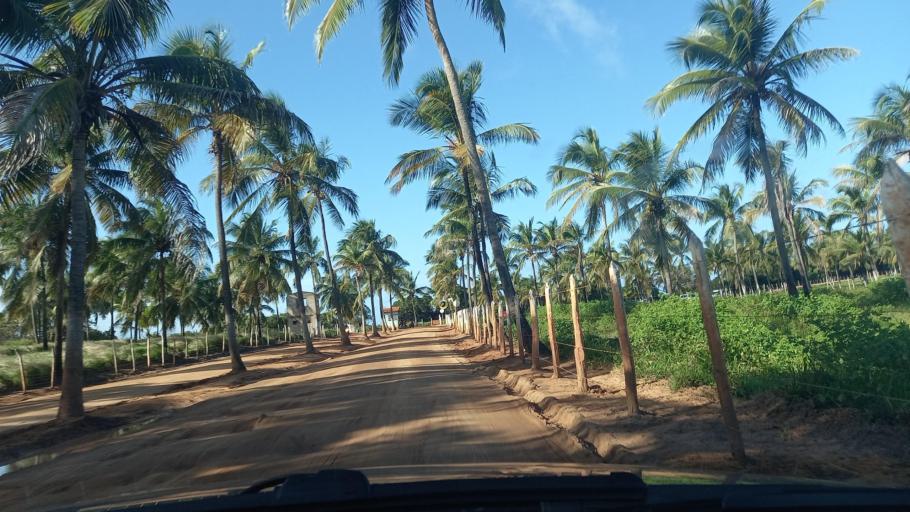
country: BR
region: Alagoas
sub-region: Marechal Deodoro
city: Marechal Deodoro
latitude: -9.8611
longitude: -35.9105
